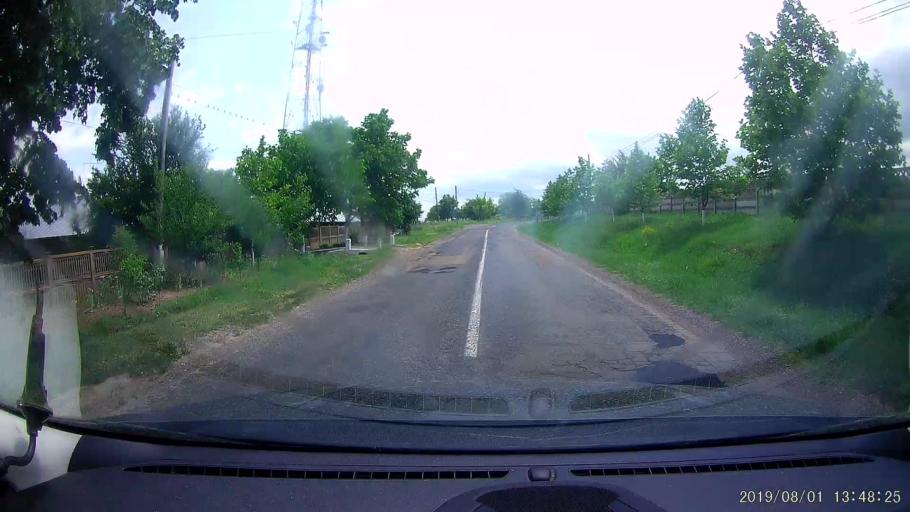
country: RO
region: Galati
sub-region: Comuna Oancea
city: Oancea
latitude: 45.9083
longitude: 28.1120
